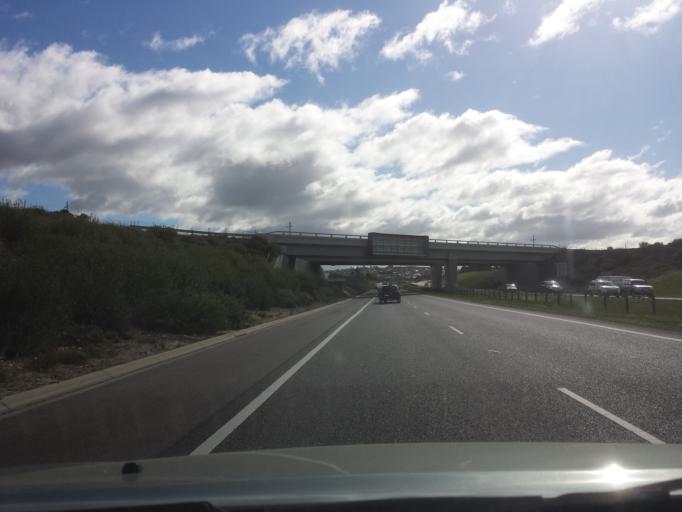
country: AU
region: Victoria
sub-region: Hume
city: Craigieburn
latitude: -37.5918
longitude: 144.9490
